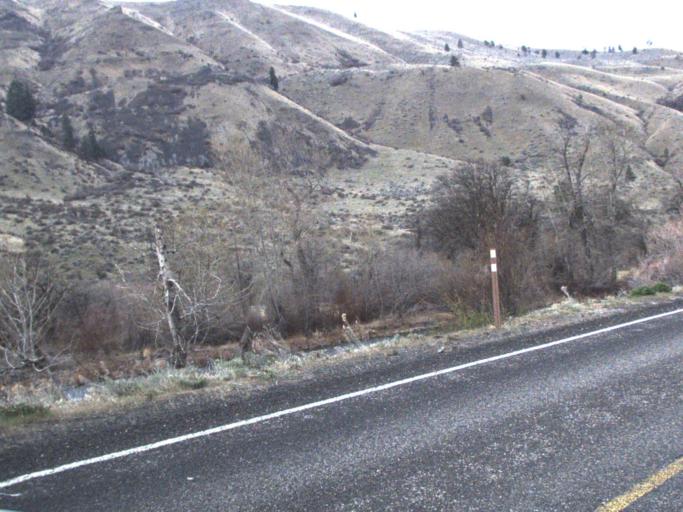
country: US
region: Washington
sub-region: Yakima County
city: Tieton
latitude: 46.7525
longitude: -120.8179
